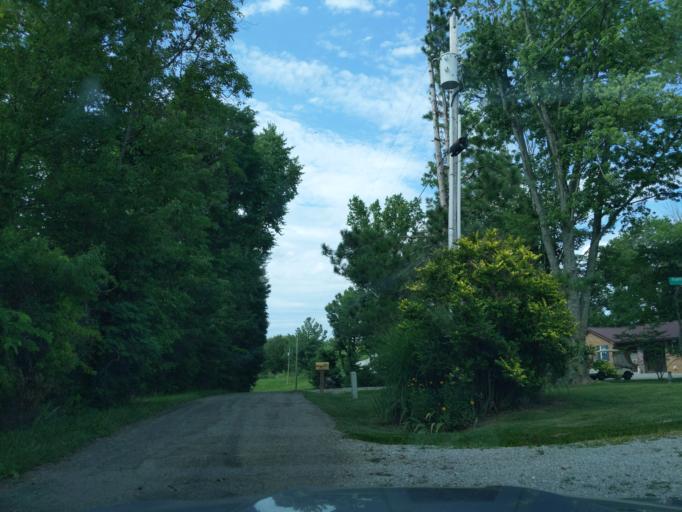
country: US
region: Indiana
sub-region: Ripley County
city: Sunman
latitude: 39.3131
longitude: -85.0996
